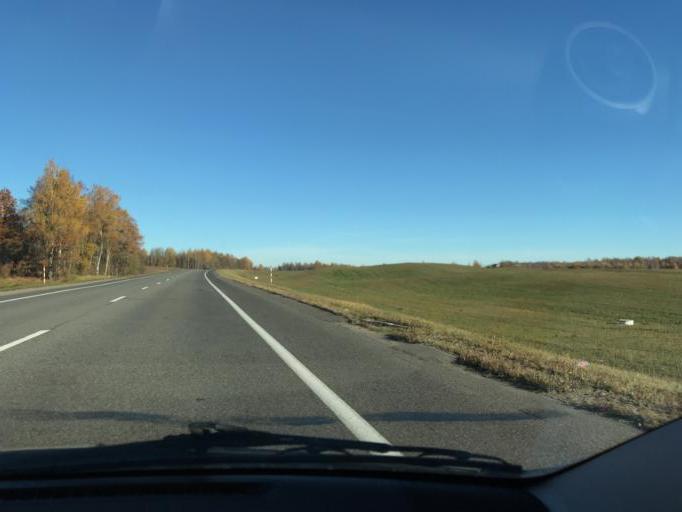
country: BY
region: Vitebsk
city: Vitebsk
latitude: 55.0718
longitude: 30.3085
